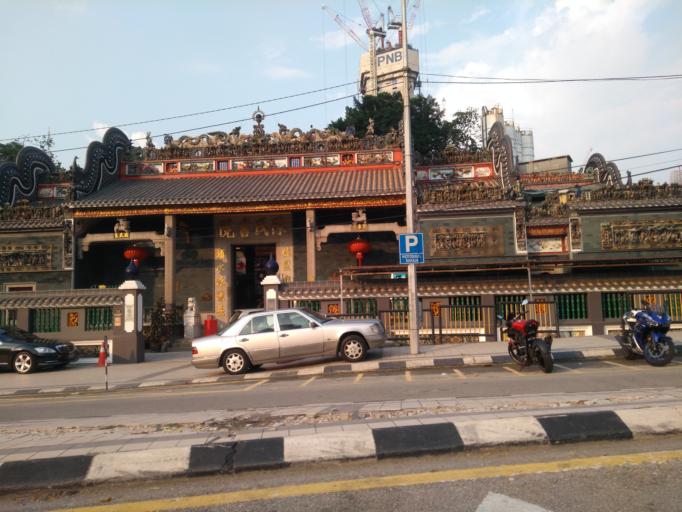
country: MY
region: Kuala Lumpur
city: Kuala Lumpur
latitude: 3.1402
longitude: 101.6982
